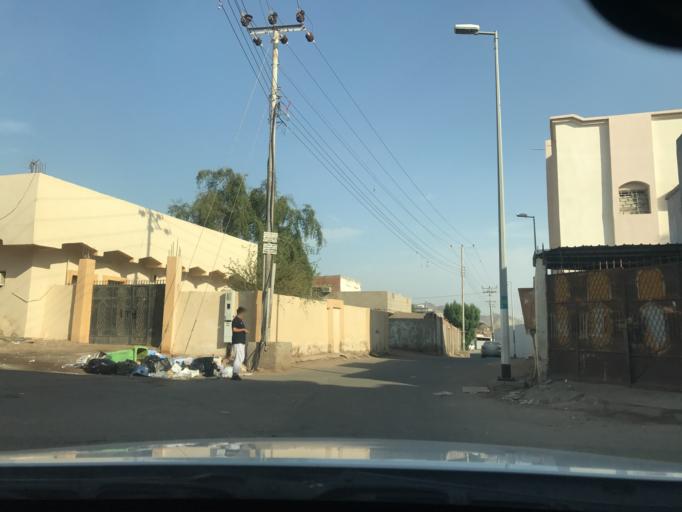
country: SA
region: Makkah
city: Al Jumum
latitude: 21.4435
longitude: 39.5349
